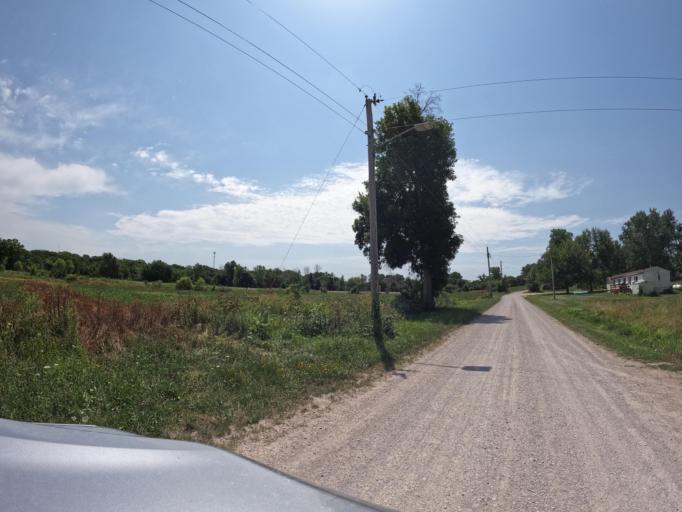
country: US
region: Iowa
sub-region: Appanoose County
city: Centerville
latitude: 40.7745
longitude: -92.9492
